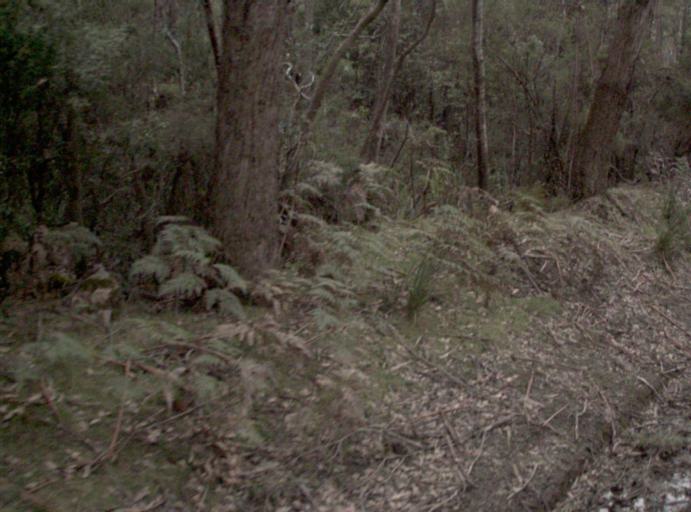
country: AU
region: Tasmania
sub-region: Launceston
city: Newstead
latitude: -41.3603
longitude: 147.2279
